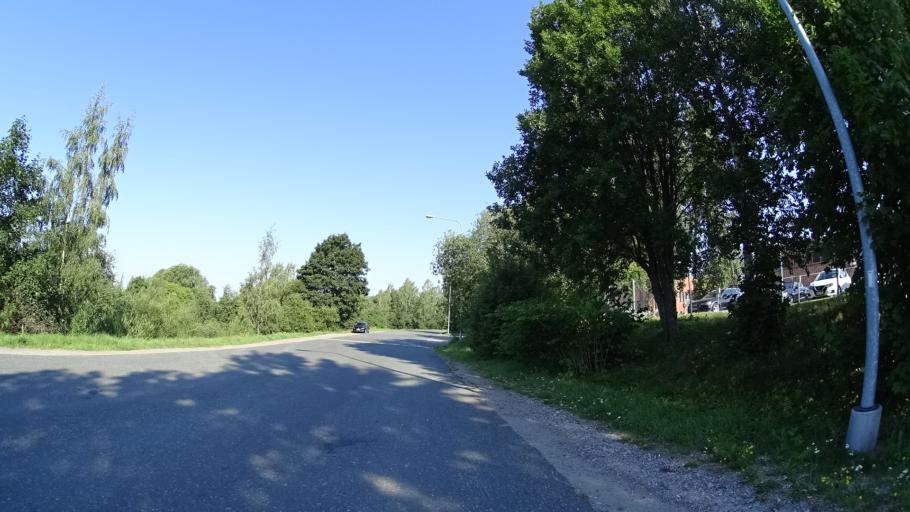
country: FI
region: Uusimaa
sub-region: Helsinki
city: Vantaa
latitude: 60.2686
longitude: 24.9783
